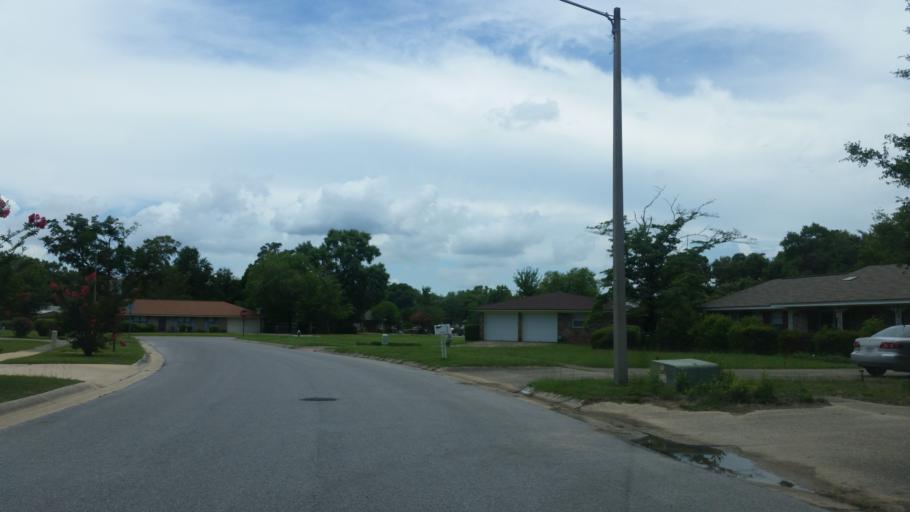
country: US
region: Florida
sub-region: Escambia County
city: Ferry Pass
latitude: 30.5128
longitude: -87.1866
